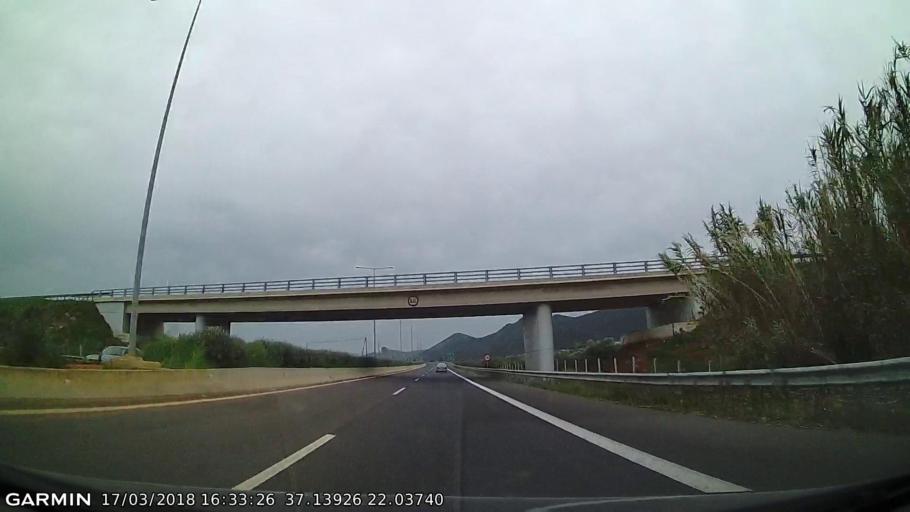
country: GR
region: Peloponnese
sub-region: Nomos Messinias
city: Arfara
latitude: 37.1394
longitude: 22.0374
